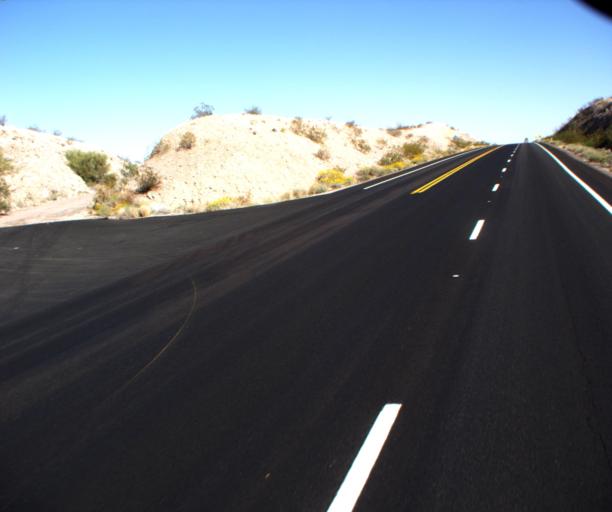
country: US
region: Arizona
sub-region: La Paz County
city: Quartzsite
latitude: 33.2413
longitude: -114.2484
